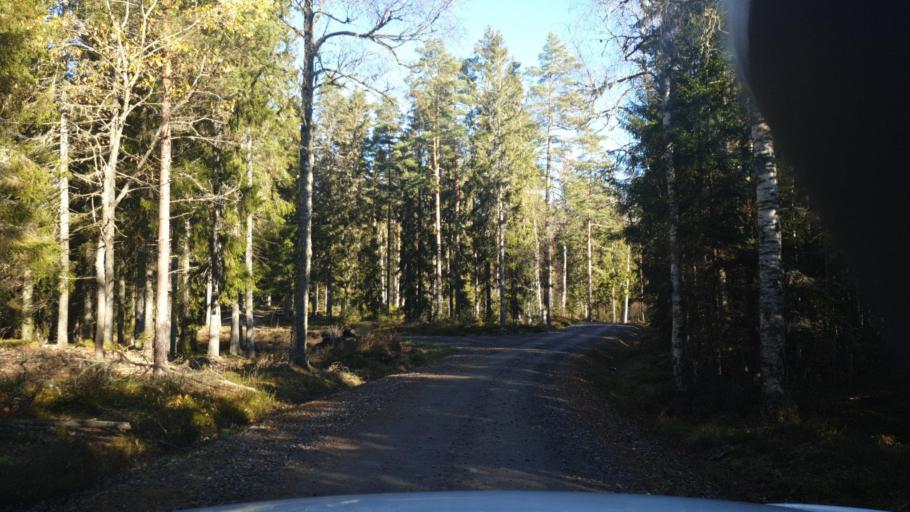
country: SE
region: Vaermland
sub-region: Karlstads Kommun
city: Edsvalla
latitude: 59.4613
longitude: 13.1010
